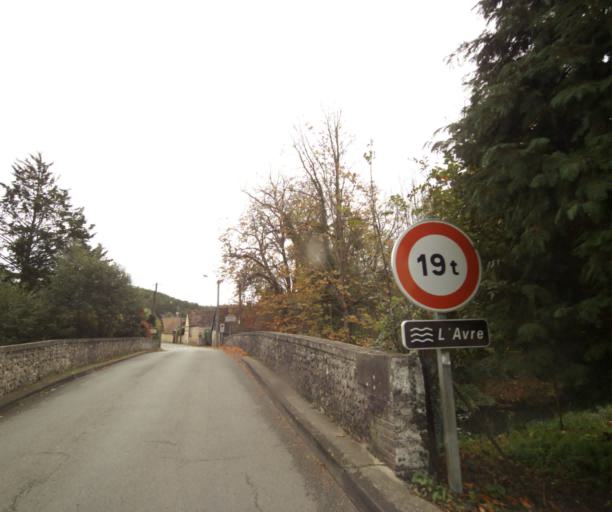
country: FR
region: Centre
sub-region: Departement d'Eure-et-Loir
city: Dreux
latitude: 48.7746
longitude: 1.3464
